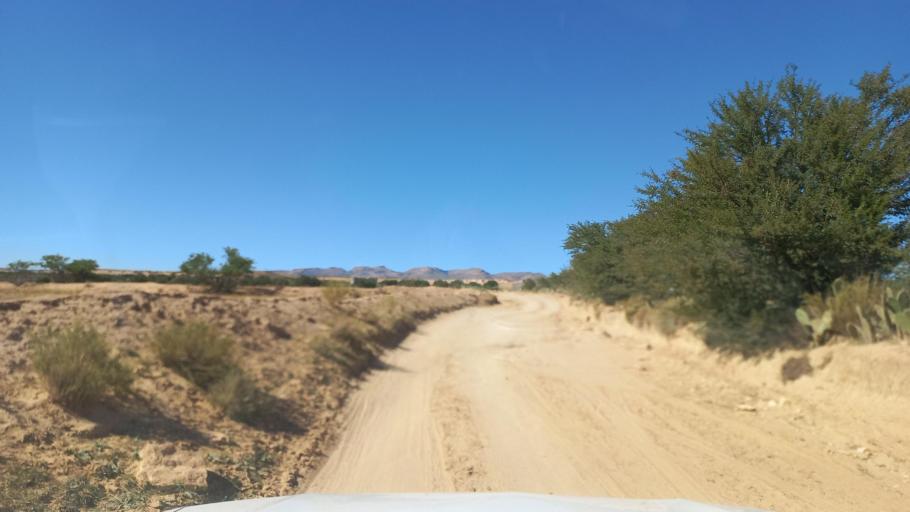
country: TN
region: Al Qasrayn
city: Sbiba
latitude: 35.3746
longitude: 9.0927
